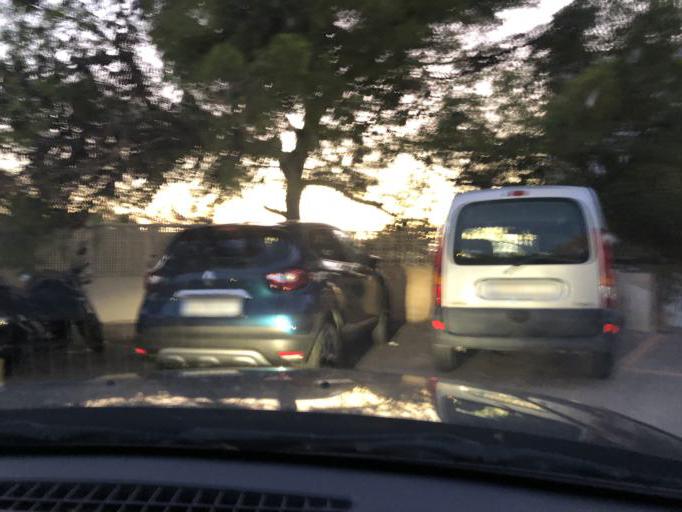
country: ES
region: Balearic Islands
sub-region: Illes Balears
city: Santa Ponsa
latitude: 39.5202
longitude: 2.4742
